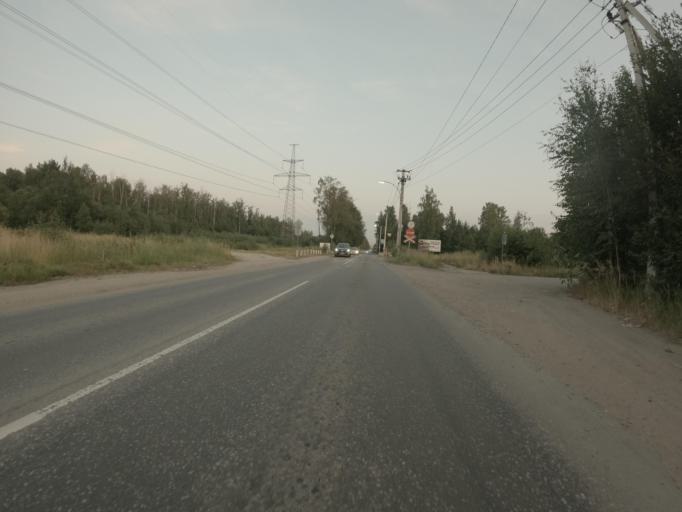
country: RU
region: St.-Petersburg
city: Krasnogvargeisky
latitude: 59.9437
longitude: 30.5215
